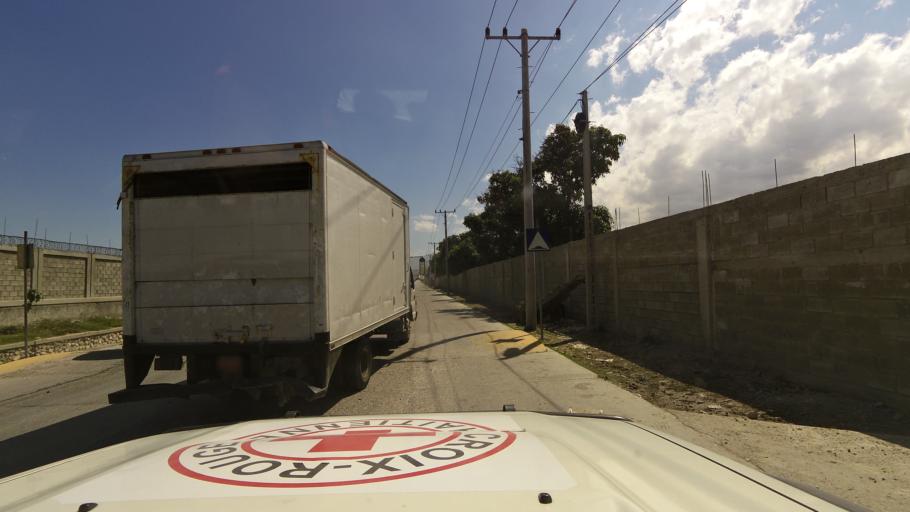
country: HT
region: Ouest
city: Delmas 73
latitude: 18.5862
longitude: -72.3173
